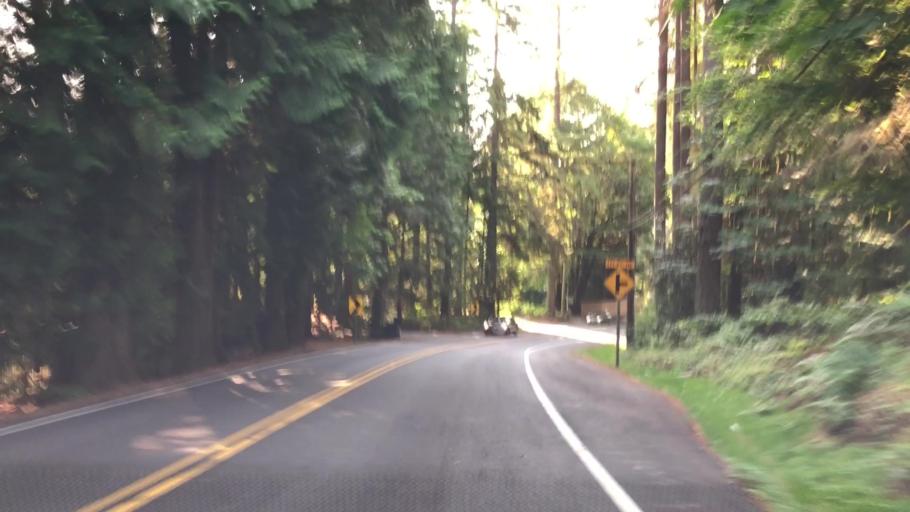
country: US
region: Washington
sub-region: King County
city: Cottage Lake
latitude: 47.7516
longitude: -122.1108
